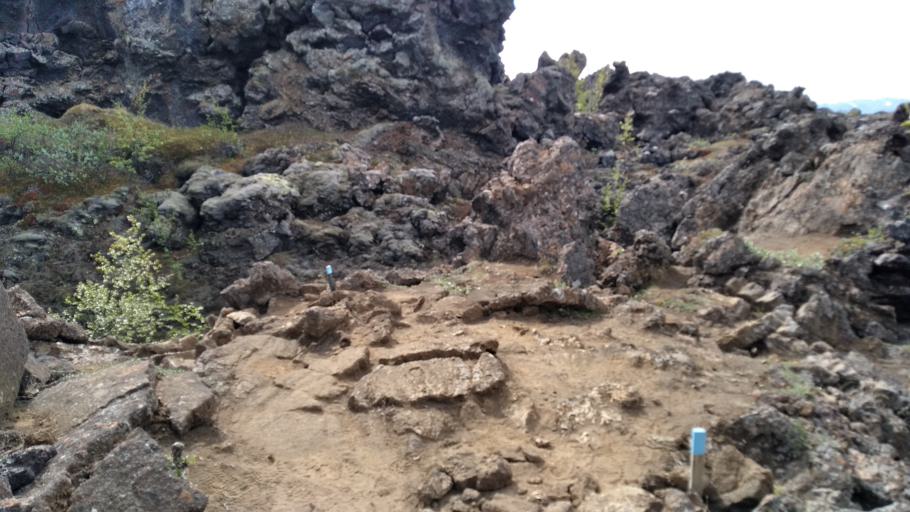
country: IS
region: Northeast
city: Laugar
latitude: 65.5885
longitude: -16.9105
